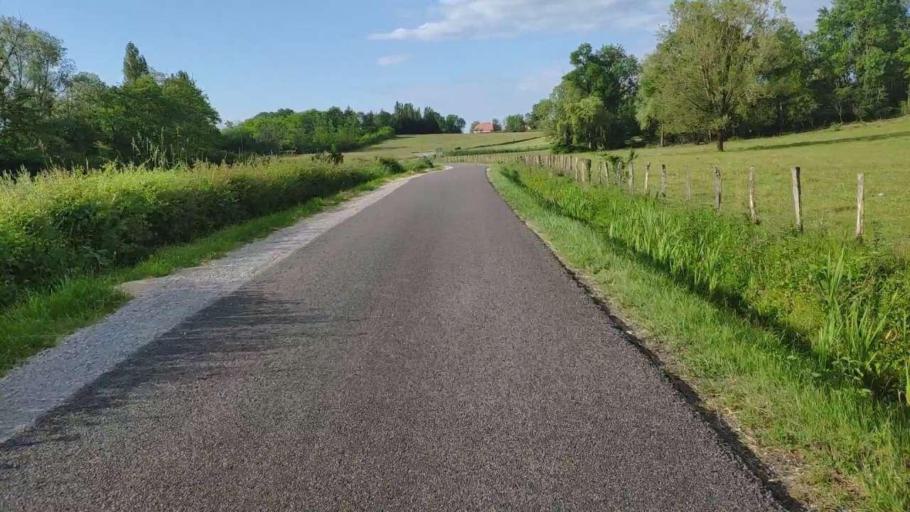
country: FR
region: Franche-Comte
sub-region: Departement du Jura
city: Bletterans
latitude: 46.7538
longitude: 5.4489
